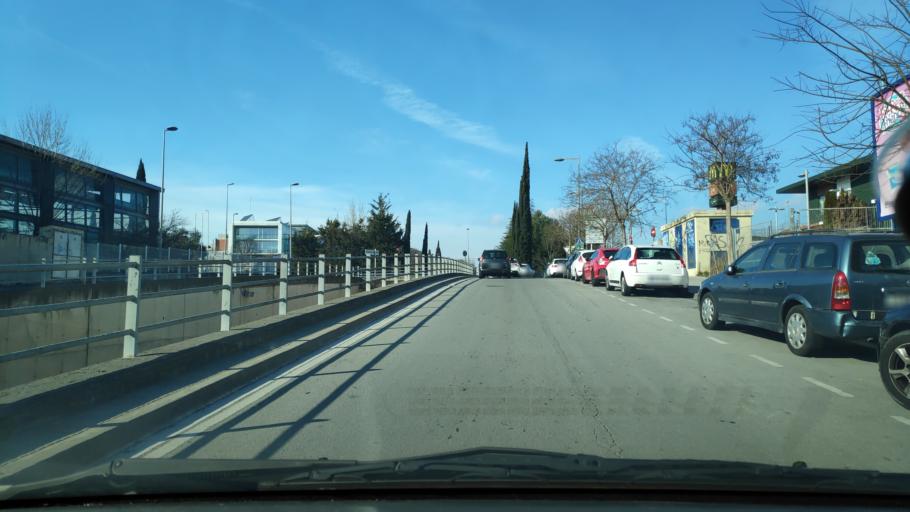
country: ES
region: Catalonia
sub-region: Provincia de Barcelona
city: Sant Cugat del Valles
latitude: 41.4766
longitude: 2.0973
